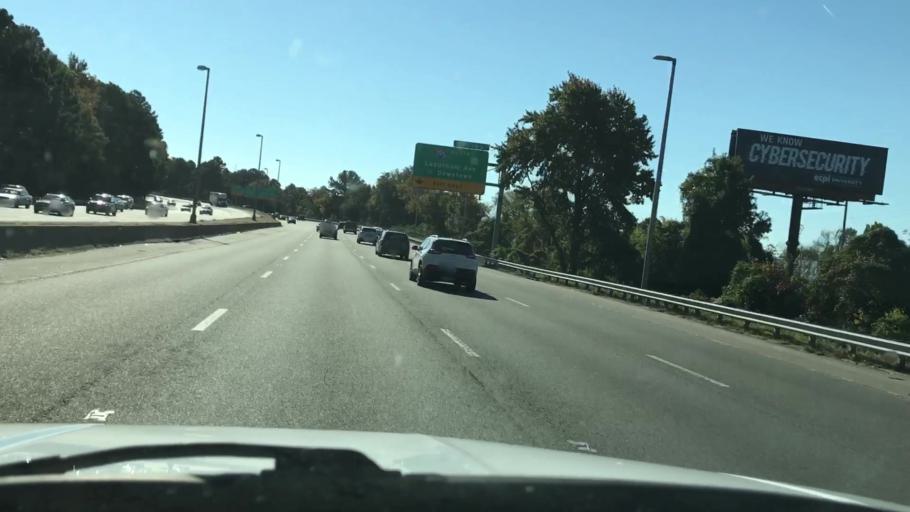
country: US
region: Virginia
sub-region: Henrico County
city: Lakeside
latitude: 37.5912
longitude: -77.4802
